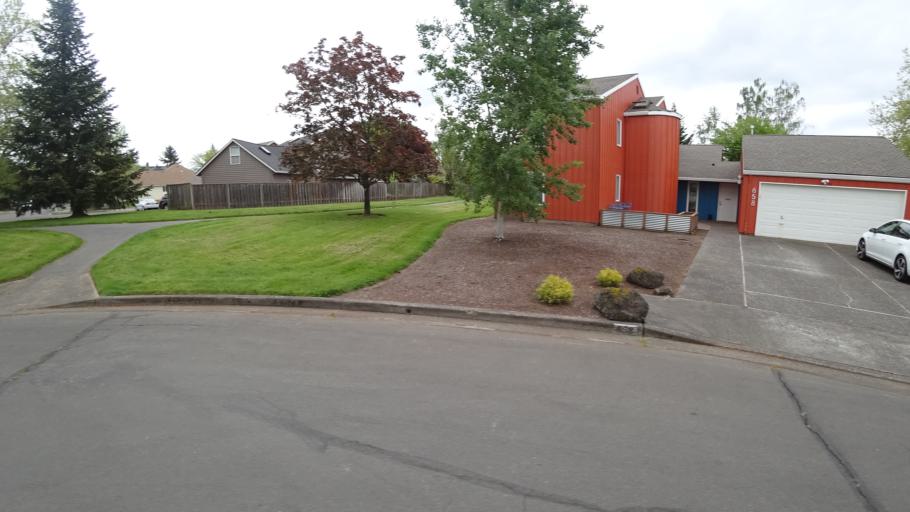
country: US
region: Oregon
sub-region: Washington County
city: Hillsboro
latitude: 45.5402
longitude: -122.9830
